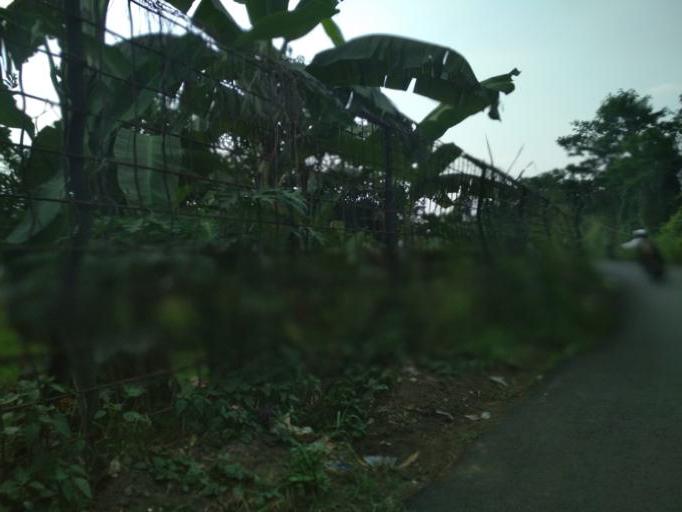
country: ID
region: West Java
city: Ciampea
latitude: -6.5646
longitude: 106.7353
